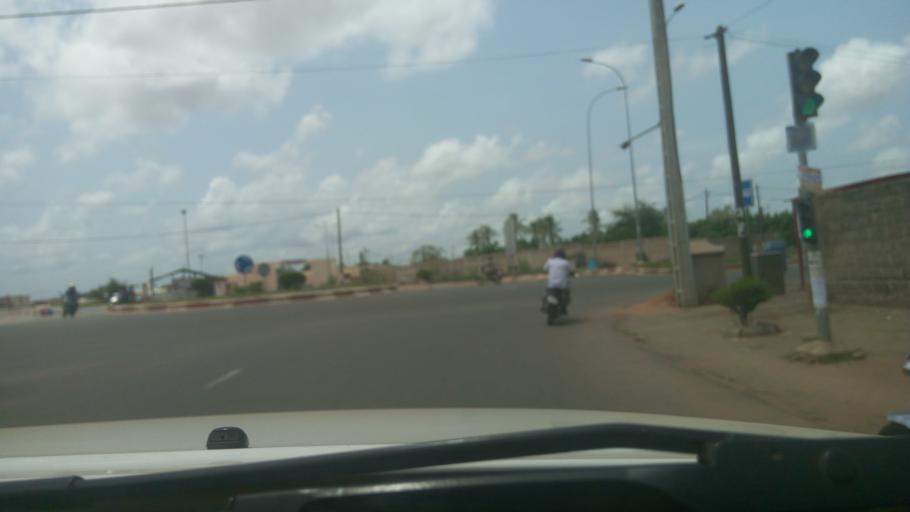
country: TG
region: Maritime
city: Lome
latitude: 6.2072
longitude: 1.1894
